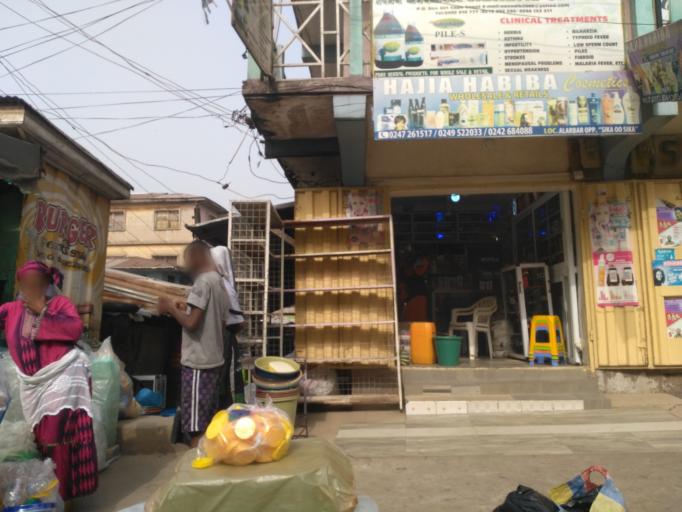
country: GH
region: Ashanti
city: Kumasi
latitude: 6.6985
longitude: -1.6145
